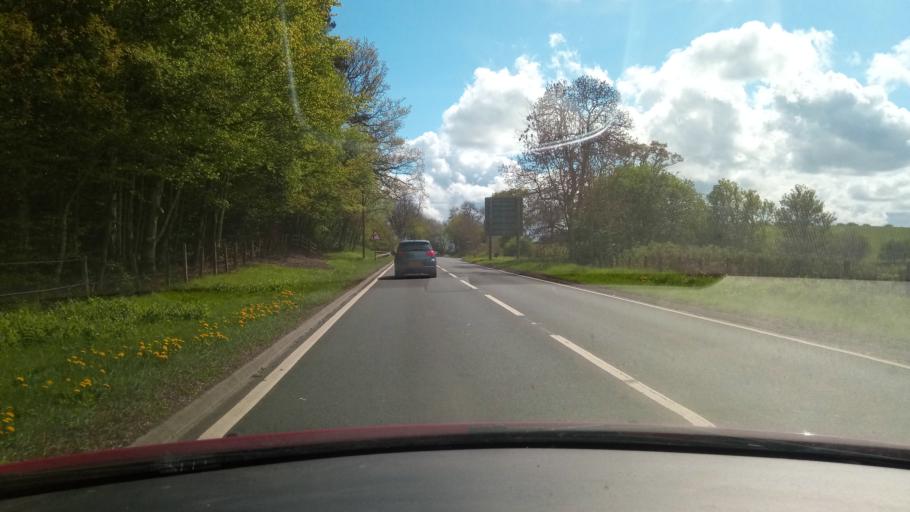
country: GB
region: Scotland
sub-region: The Scottish Borders
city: Newtown St Boswells
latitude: 55.5939
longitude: -2.6705
